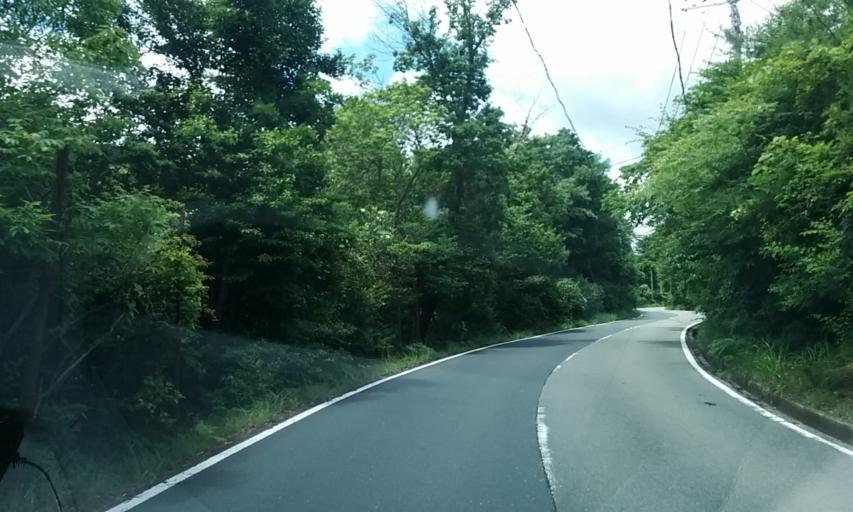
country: JP
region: Kyoto
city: Kameoka
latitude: 35.0097
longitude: 135.4633
